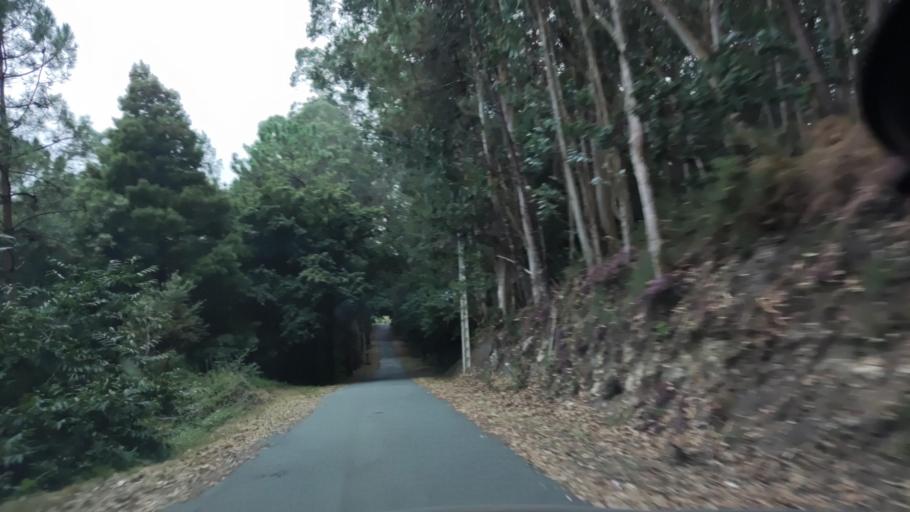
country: ES
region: Galicia
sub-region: Provincia de Pontevedra
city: Catoira
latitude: 42.7029
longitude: -8.7252
